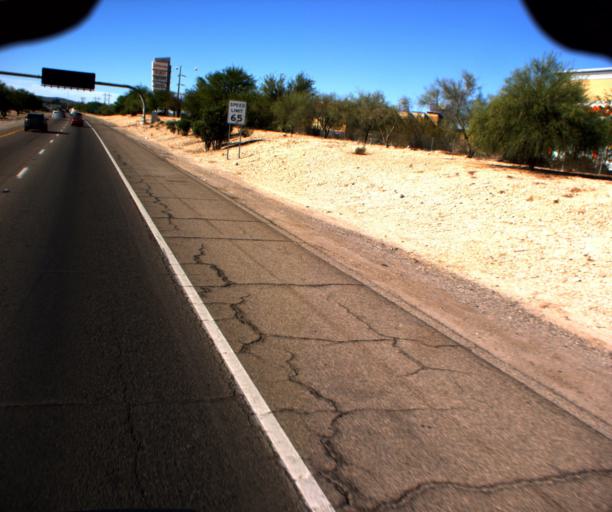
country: US
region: Arizona
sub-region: Pima County
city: Drexel Heights
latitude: 32.1541
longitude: -110.9867
